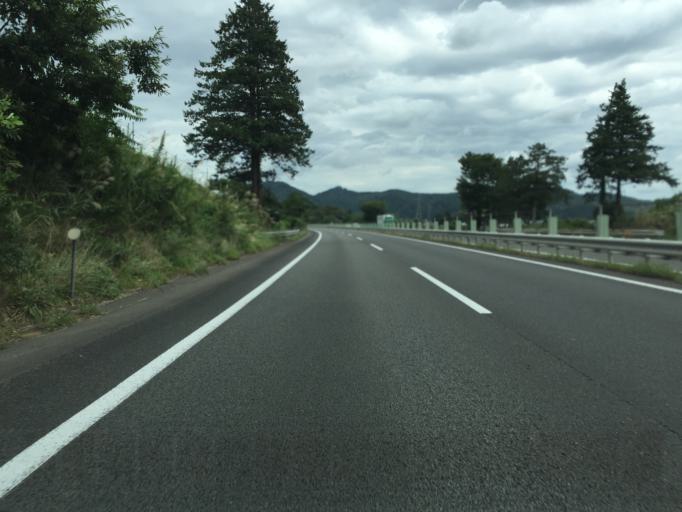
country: JP
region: Miyagi
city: Shiroishi
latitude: 38.0462
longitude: 140.6461
